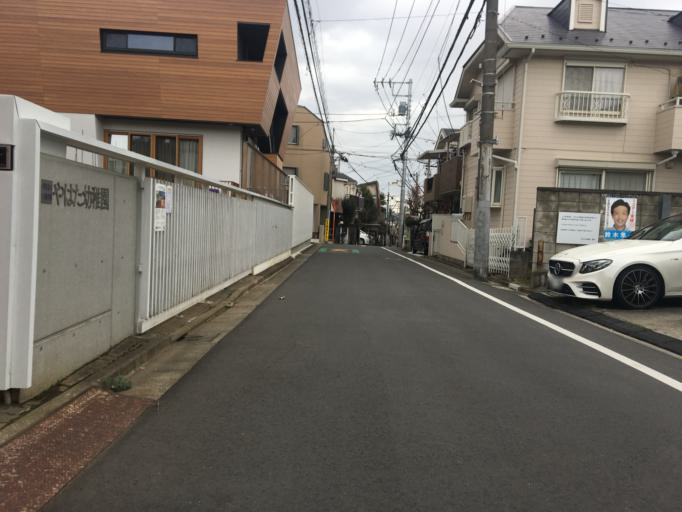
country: JP
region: Tokyo
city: Tokyo
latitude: 35.7142
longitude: 139.6510
